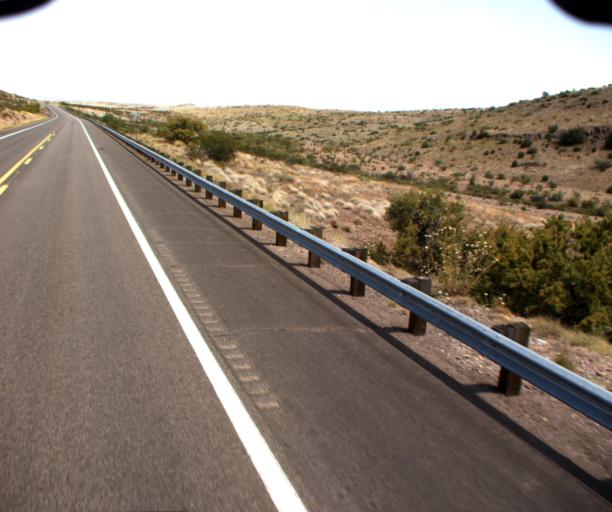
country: US
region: Arizona
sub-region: Greenlee County
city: Clifton
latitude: 32.7375
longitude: -109.1999
